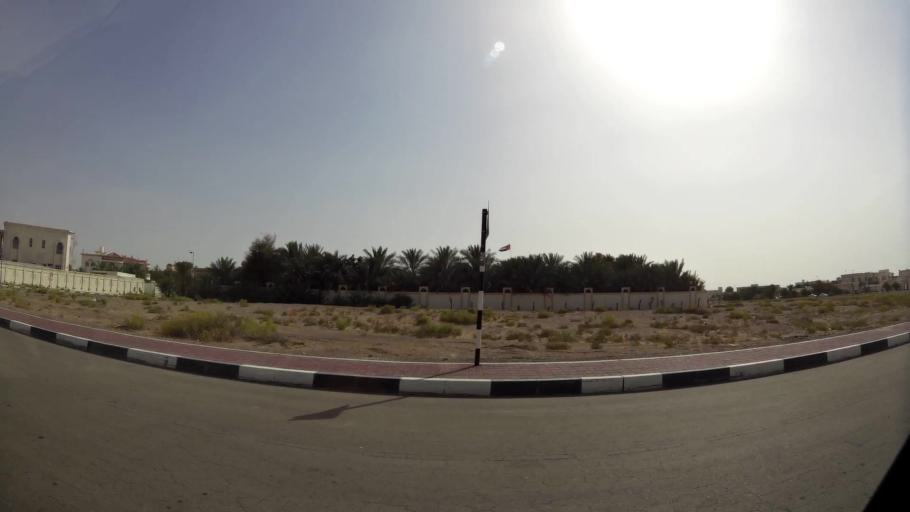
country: AE
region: Abu Dhabi
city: Al Ain
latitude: 24.2343
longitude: 55.6735
